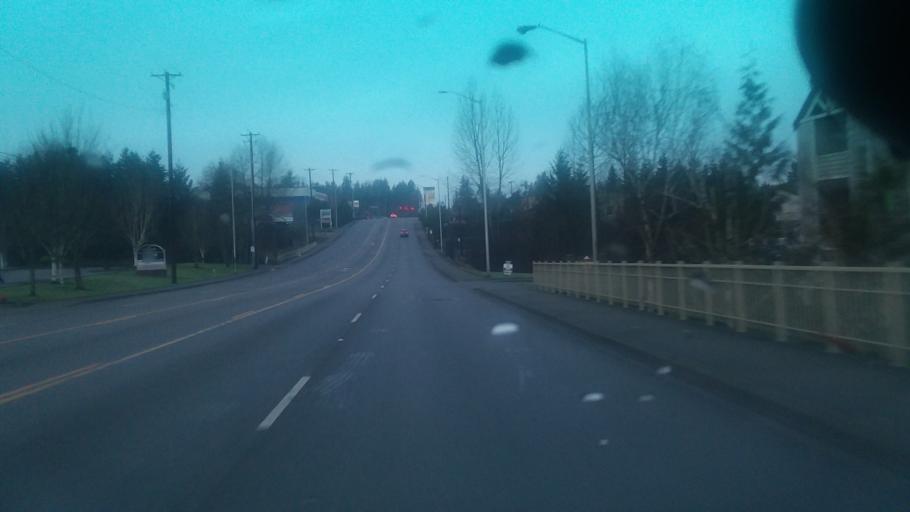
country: US
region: Washington
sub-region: Pierce County
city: Summit
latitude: 47.1546
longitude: -122.3522
